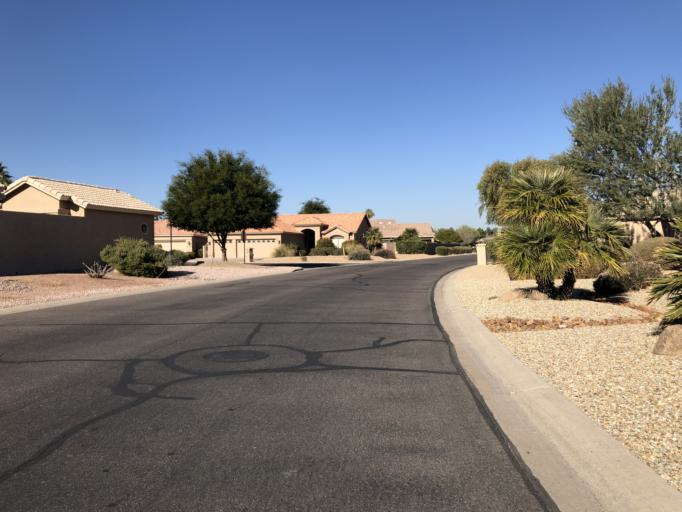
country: US
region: Arizona
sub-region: Maricopa County
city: Sun Lakes
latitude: 33.2286
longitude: -111.8768
